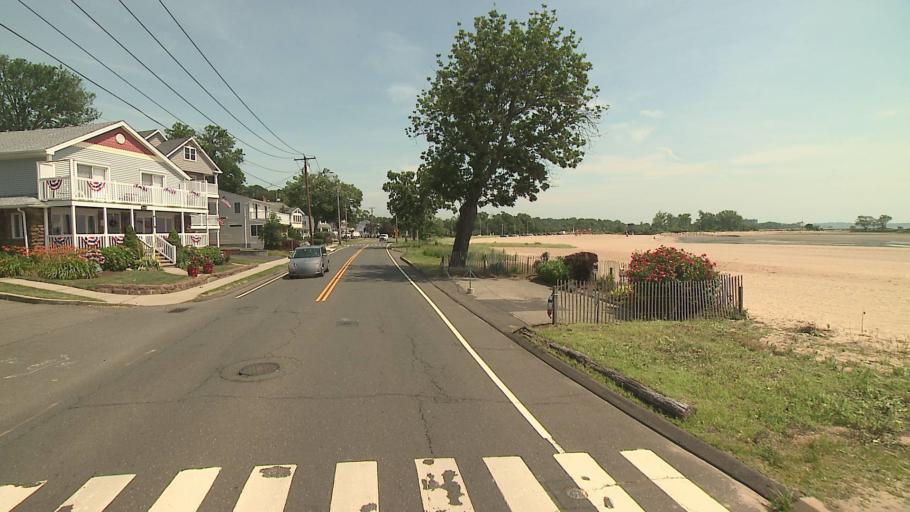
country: US
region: Connecticut
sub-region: New Haven County
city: West Haven
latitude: 41.2502
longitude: -72.9632
